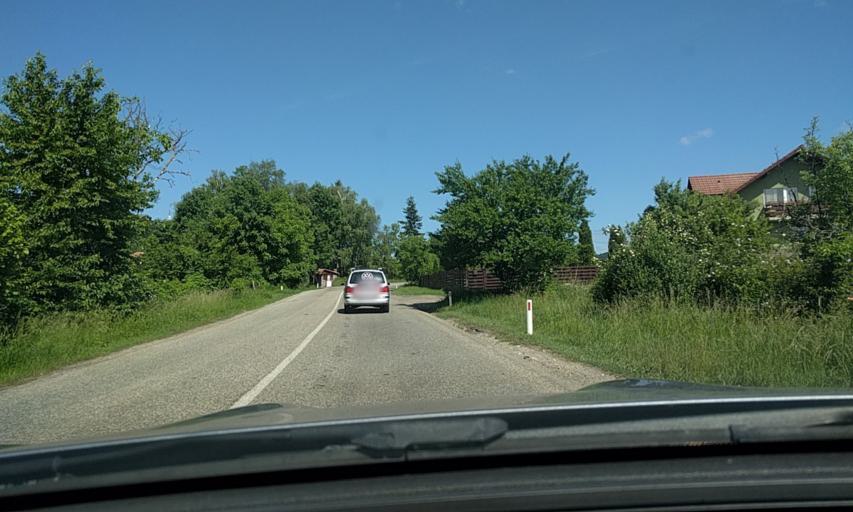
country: RO
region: Bistrita-Nasaud
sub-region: Municipiul Bistrita
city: Unirea
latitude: 47.1653
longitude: 24.5010
